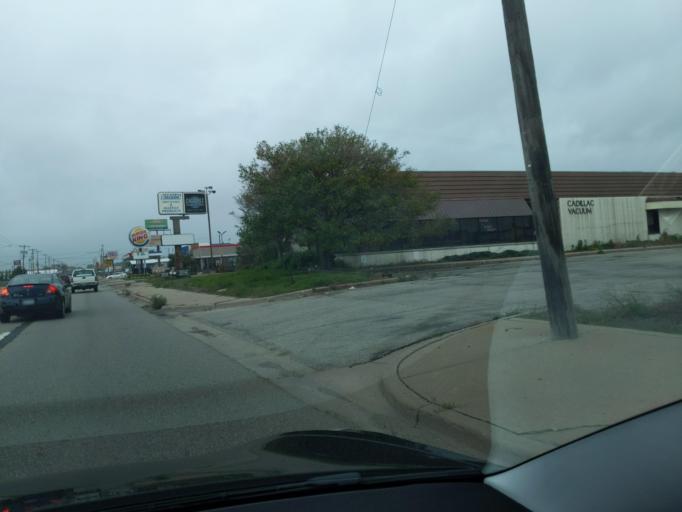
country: US
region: Michigan
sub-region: Wexford County
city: Cadillac
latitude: 44.2717
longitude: -85.4065
